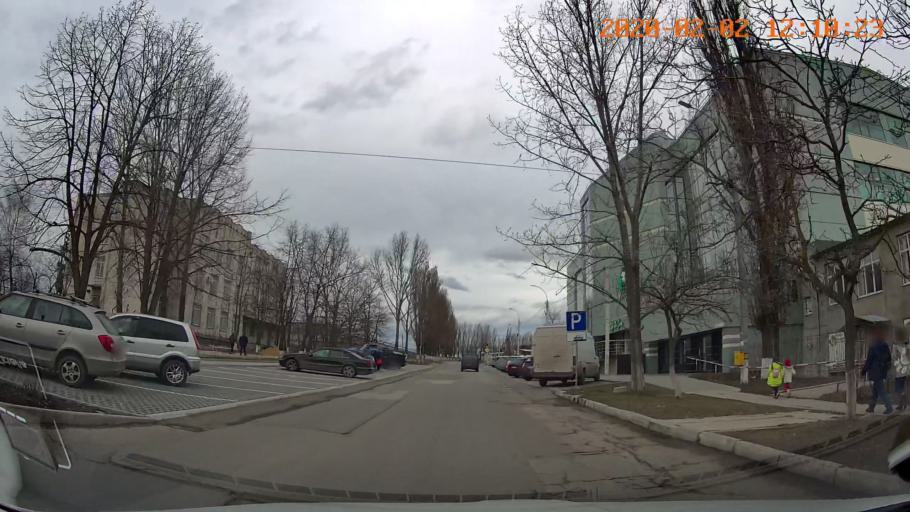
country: MD
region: Chisinau
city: Chisinau
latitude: 46.9998
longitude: 28.8042
